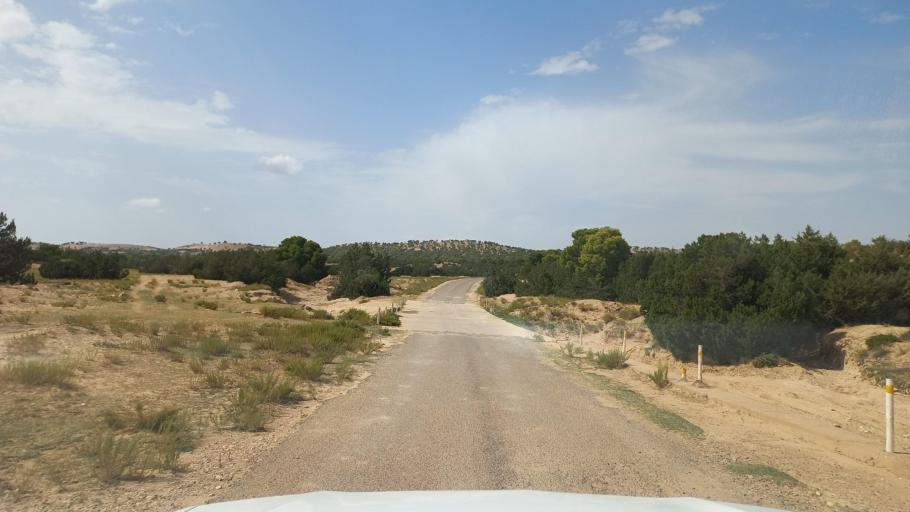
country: TN
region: Al Qasrayn
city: Sbiba
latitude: 35.4101
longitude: 8.9296
